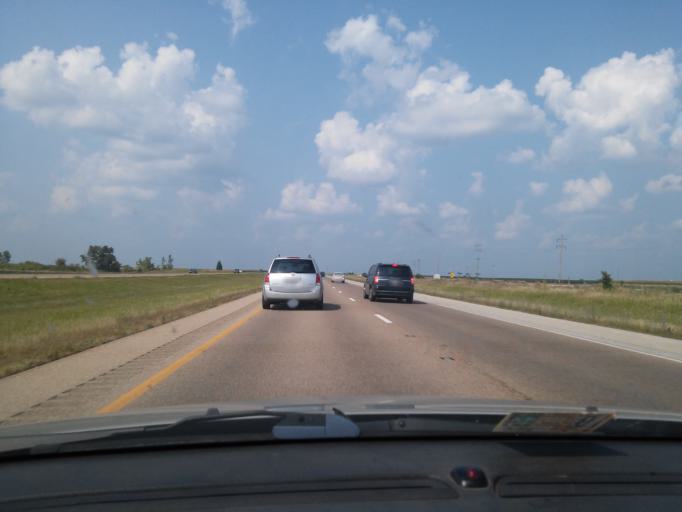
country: US
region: Illinois
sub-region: McLean County
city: Chenoa
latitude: 40.6956
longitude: -88.7522
